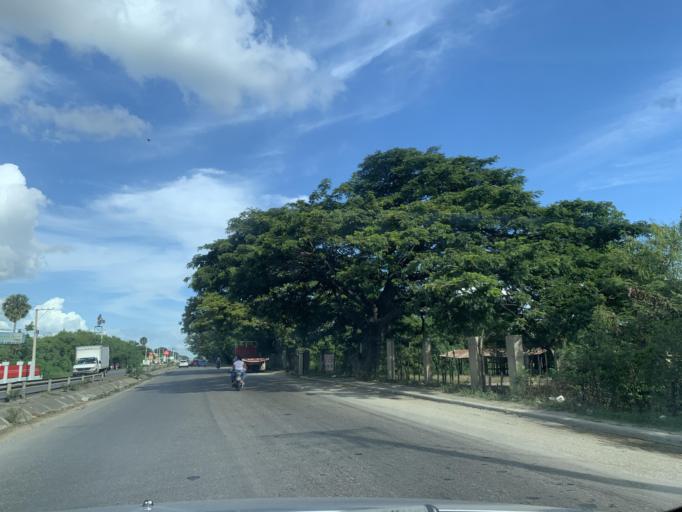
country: DO
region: Santiago
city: Villa Gonzalez
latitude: 19.5462
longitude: -70.8064
